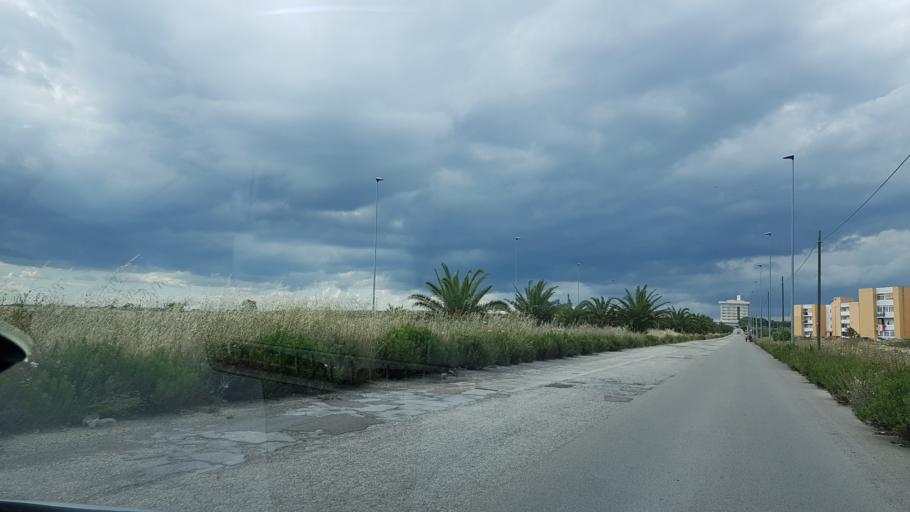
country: IT
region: Apulia
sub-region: Provincia di Taranto
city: Paolo VI
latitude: 40.5302
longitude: 17.2770
